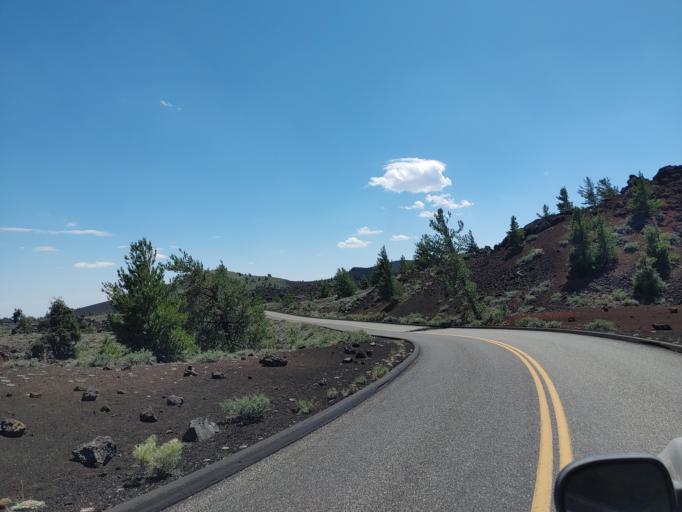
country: US
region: Idaho
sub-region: Butte County
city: Arco
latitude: 43.4599
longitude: -113.5574
